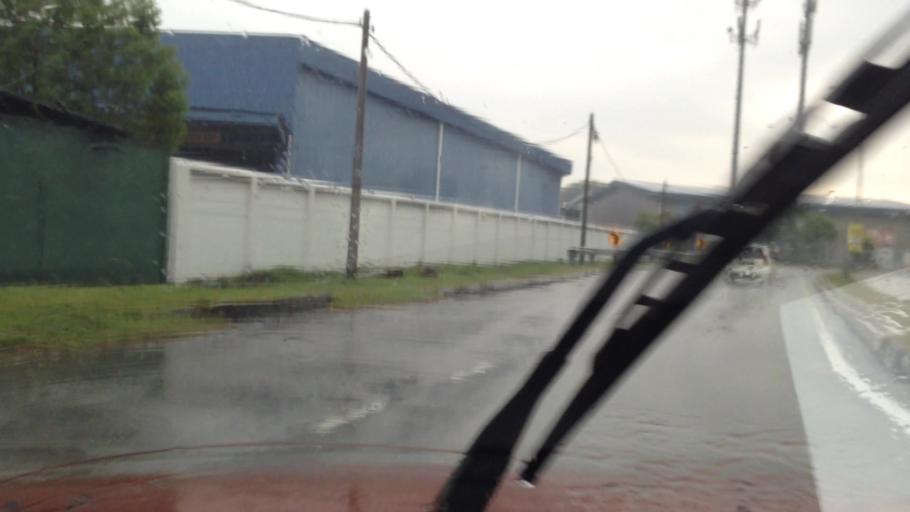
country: MY
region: Selangor
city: Subang Jaya
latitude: 3.0265
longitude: 101.5893
